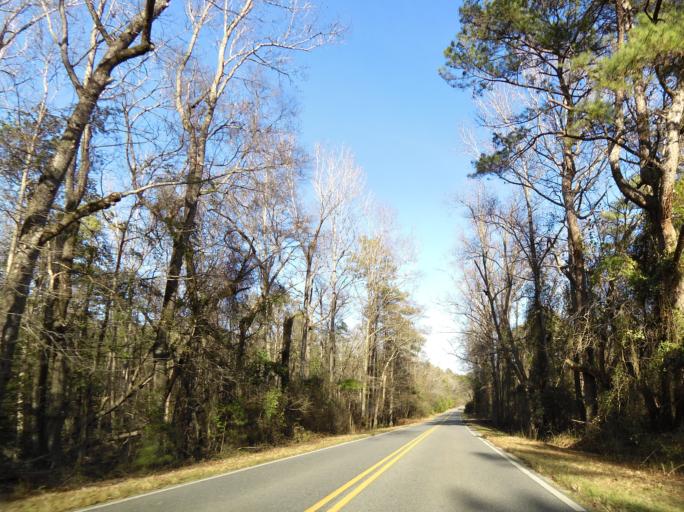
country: US
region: Georgia
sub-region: Bibb County
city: West Point
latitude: 32.7816
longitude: -83.8128
